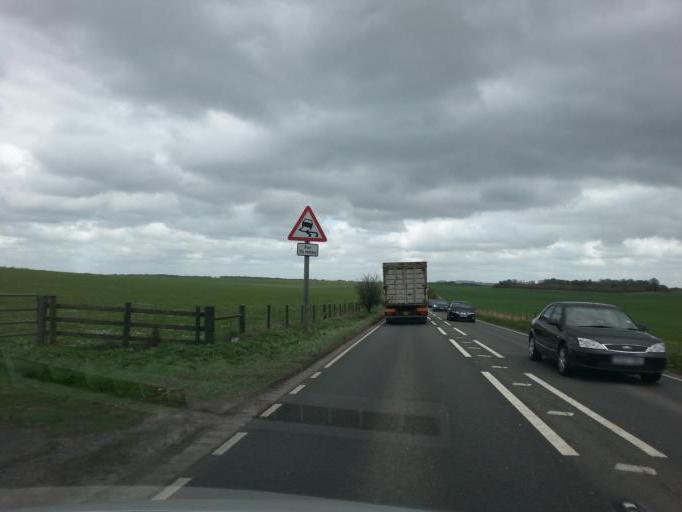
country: GB
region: England
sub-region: Wiltshire
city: Winterbourne Stoke
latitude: 51.1728
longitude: -1.8538
